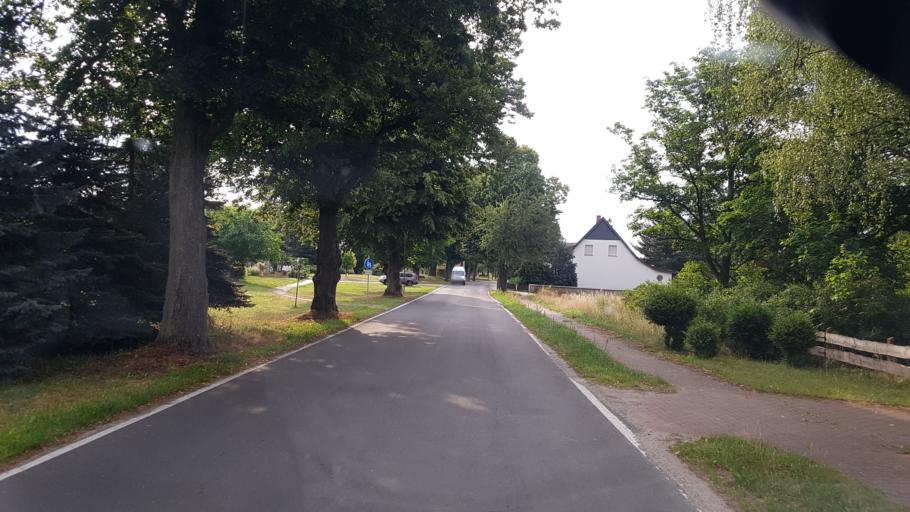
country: DE
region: Brandenburg
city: Dahme
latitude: 51.9513
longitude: 13.4682
